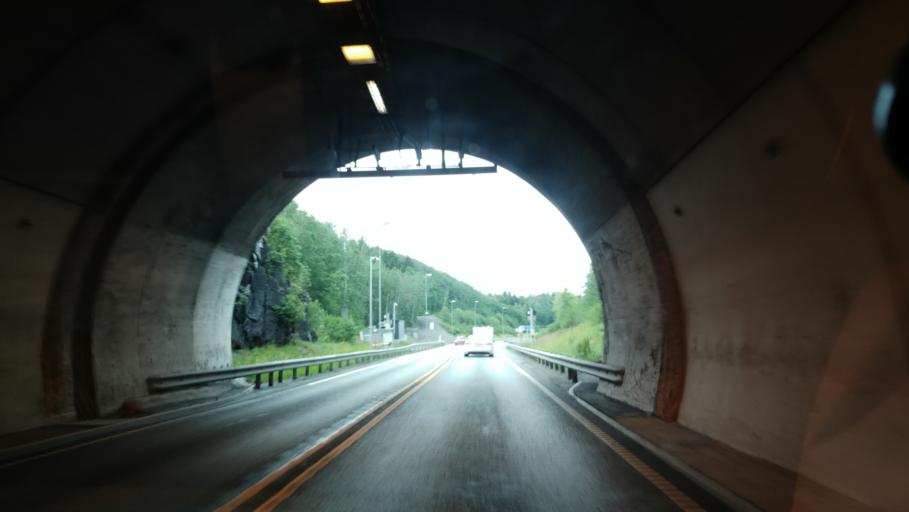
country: NO
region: Sor-Trondelag
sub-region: Malvik
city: Malvik
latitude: 63.4230
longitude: 10.5839
